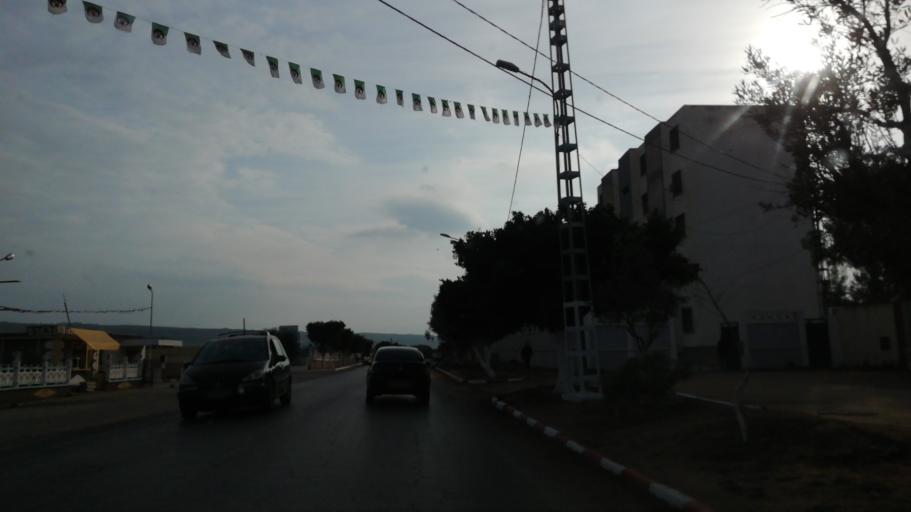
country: DZ
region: Mostaganem
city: Mostaganem
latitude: 35.8548
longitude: 0.0718
